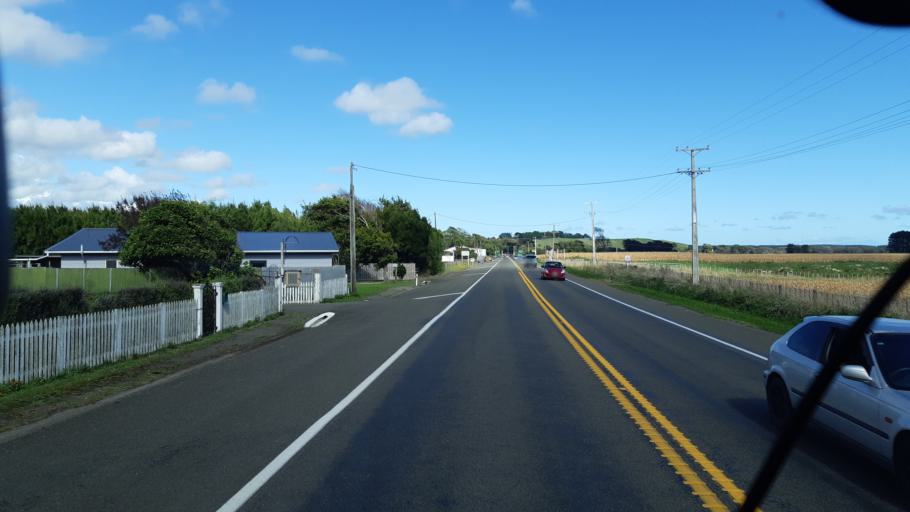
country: NZ
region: Manawatu-Wanganui
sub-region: Wanganui District
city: Wanganui
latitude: -40.0363
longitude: 175.2121
